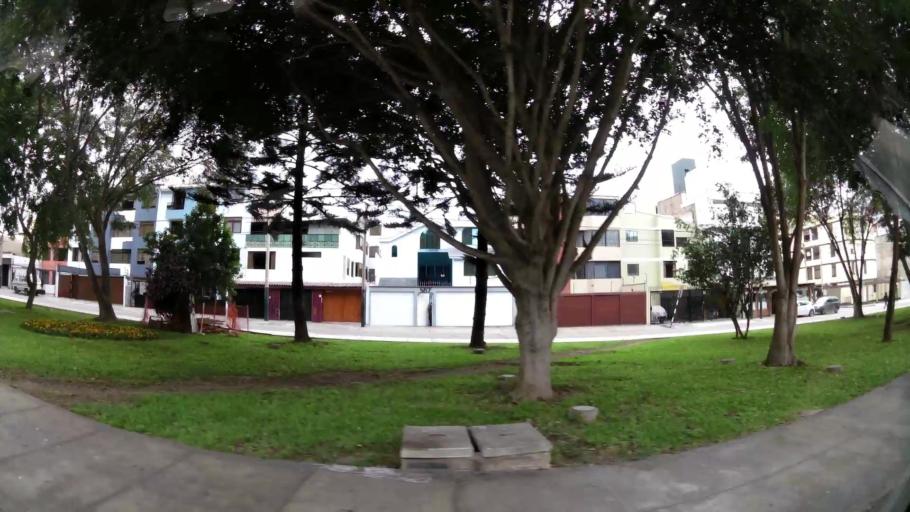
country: PE
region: Lima
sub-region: Lima
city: Surco
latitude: -12.1350
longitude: -77.0043
